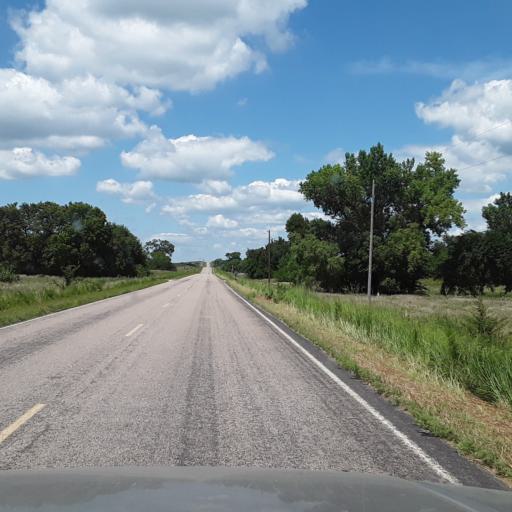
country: US
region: Nebraska
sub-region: Nance County
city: Genoa
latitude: 41.5021
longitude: -97.6959
